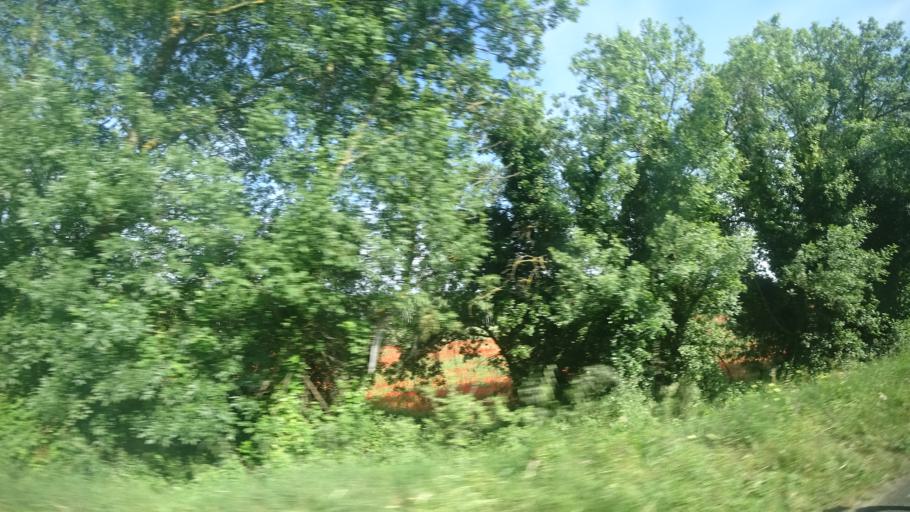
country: FR
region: Languedoc-Roussillon
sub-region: Departement de l'Aude
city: Bize-Minervois
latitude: 43.2946
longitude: 2.8682
